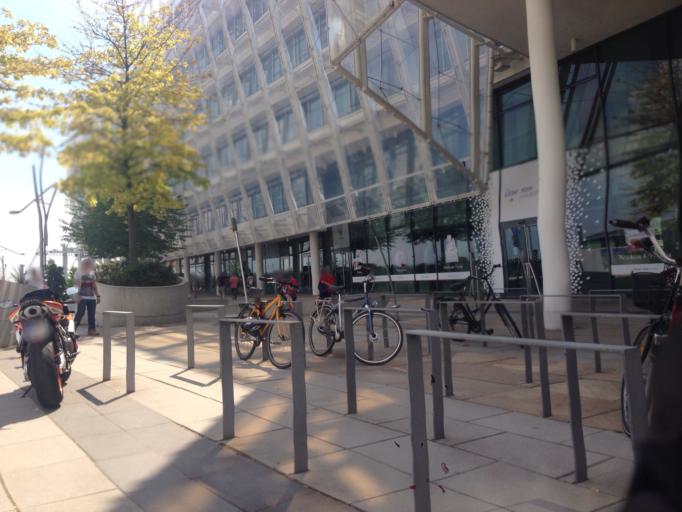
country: DE
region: Hamburg
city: Kleiner Grasbrook
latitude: 53.5397
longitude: 9.9938
